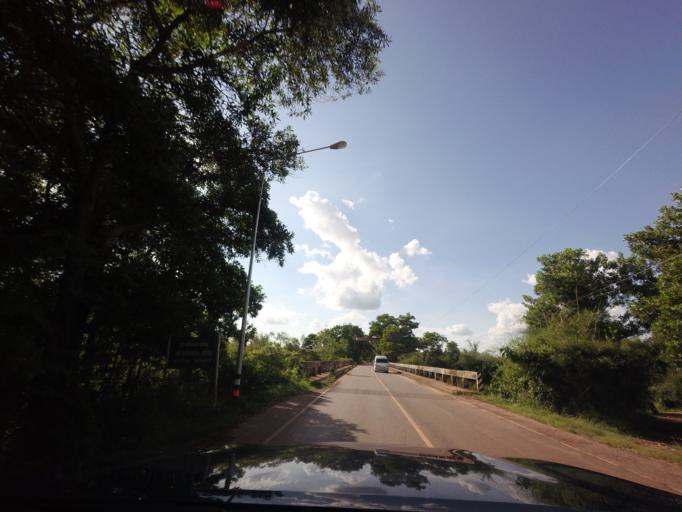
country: TH
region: Changwat Udon Thani
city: Ban Dung
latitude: 17.7424
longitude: 103.3406
